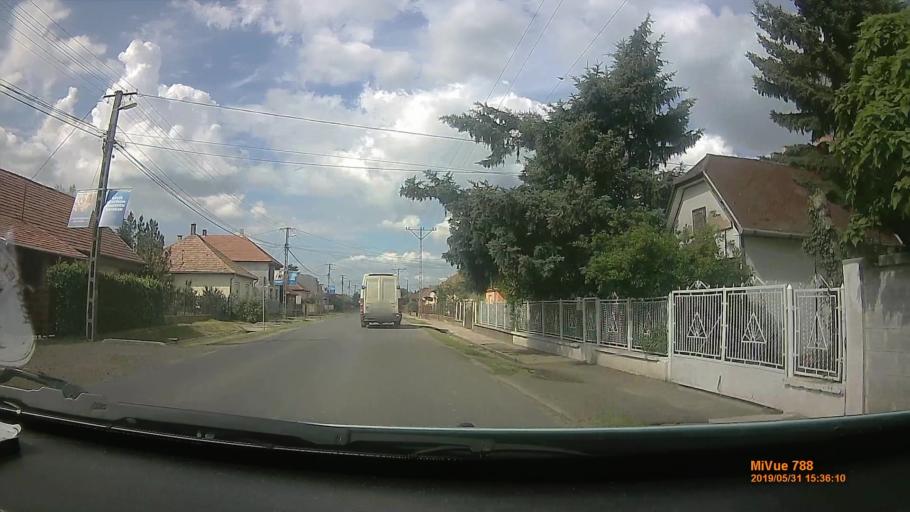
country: HU
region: Borsod-Abauj-Zemplen
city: Prugy
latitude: 48.0821
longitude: 21.2396
